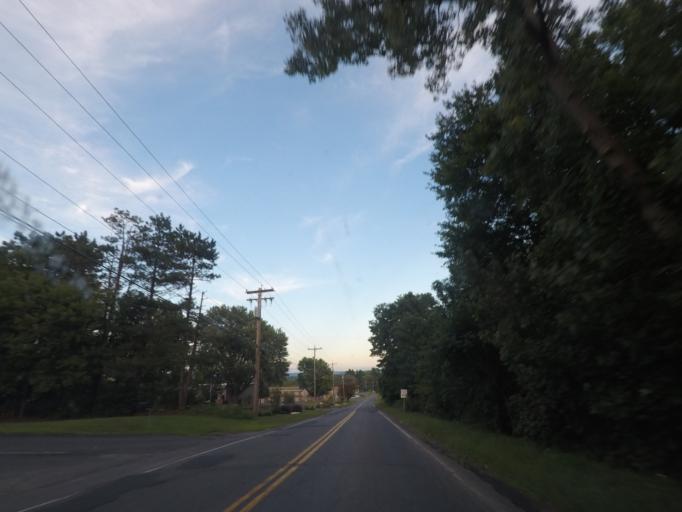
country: US
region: New York
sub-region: Schenectady County
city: Niskayuna
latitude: 42.7666
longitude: -73.7765
